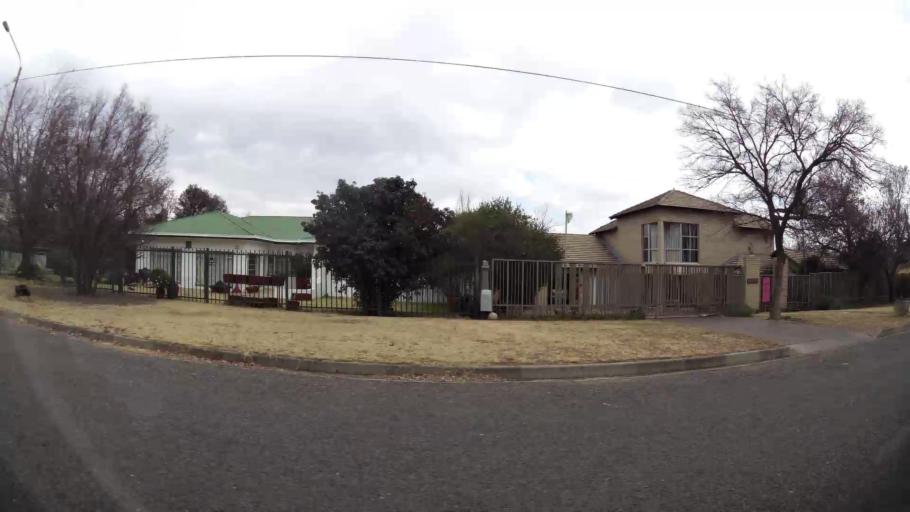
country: ZA
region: Orange Free State
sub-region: Fezile Dabi District Municipality
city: Kroonstad
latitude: -27.6802
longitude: 27.2444
